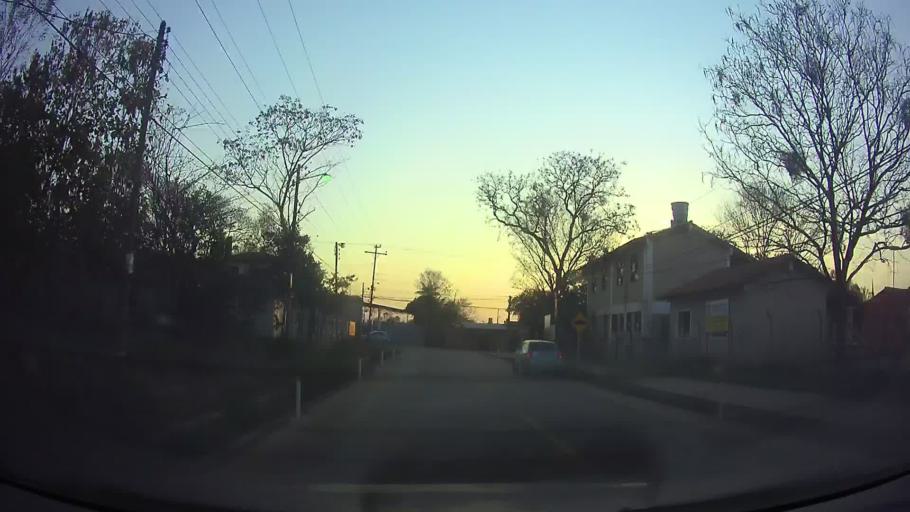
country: PY
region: Central
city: Limpio
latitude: -25.2379
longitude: -57.5085
